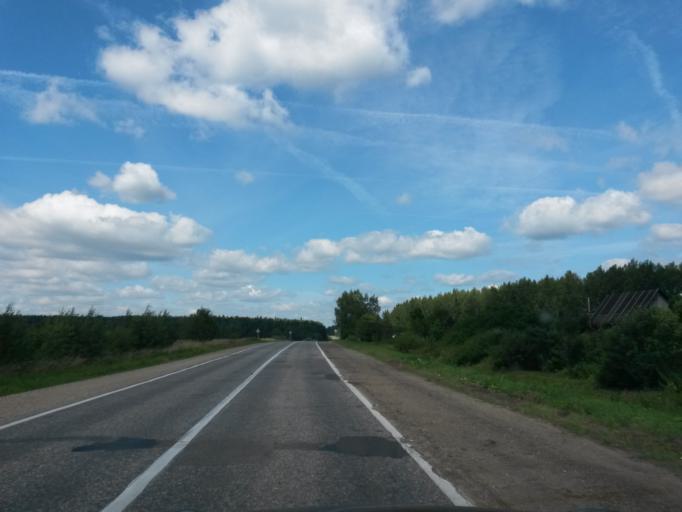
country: RU
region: Jaroslavl
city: Krasnyye Tkachi
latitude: 57.4615
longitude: 39.9088
